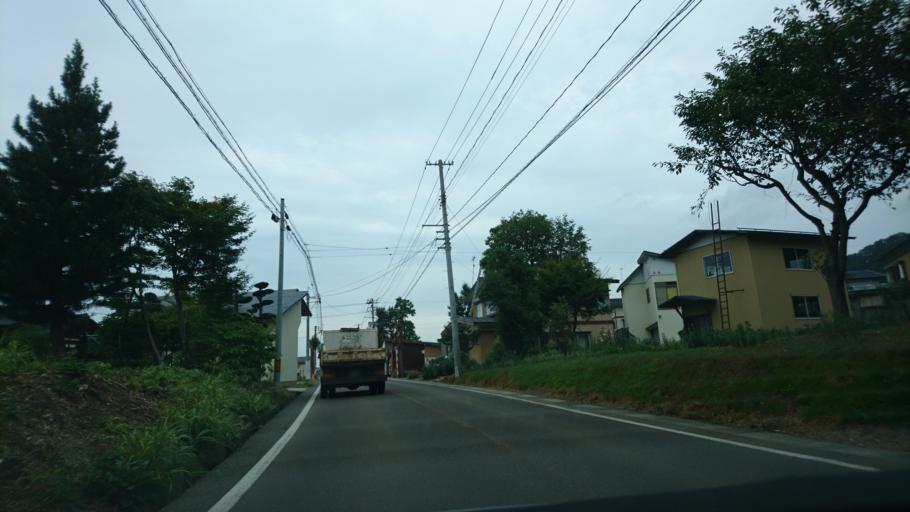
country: JP
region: Akita
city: Yuzawa
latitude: 39.1149
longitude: 140.5830
